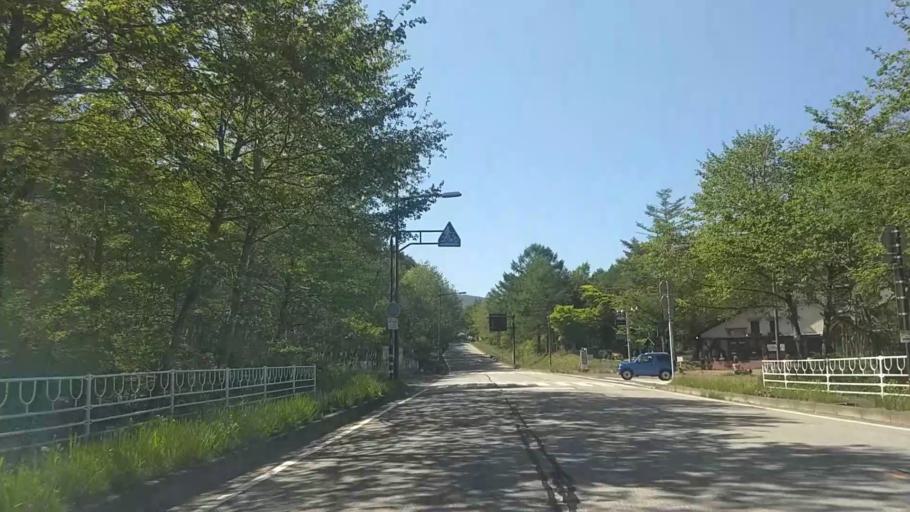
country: JP
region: Yamanashi
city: Nirasaki
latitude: 35.9217
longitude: 138.4344
